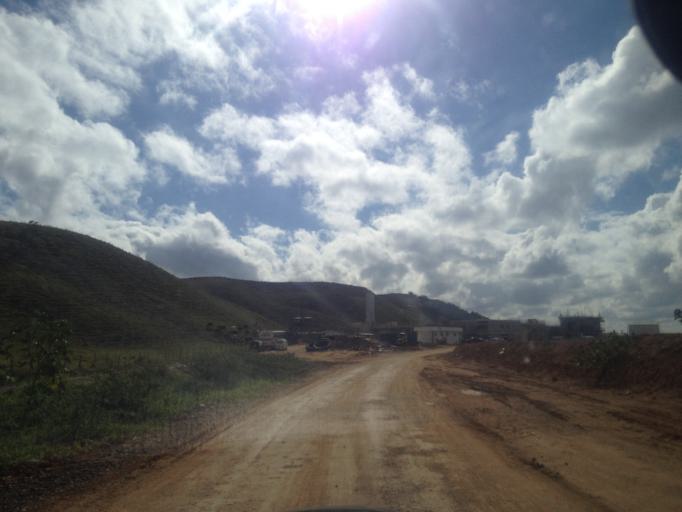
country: BR
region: Rio de Janeiro
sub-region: Resende
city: Resende
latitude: -22.4232
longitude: -44.3847
